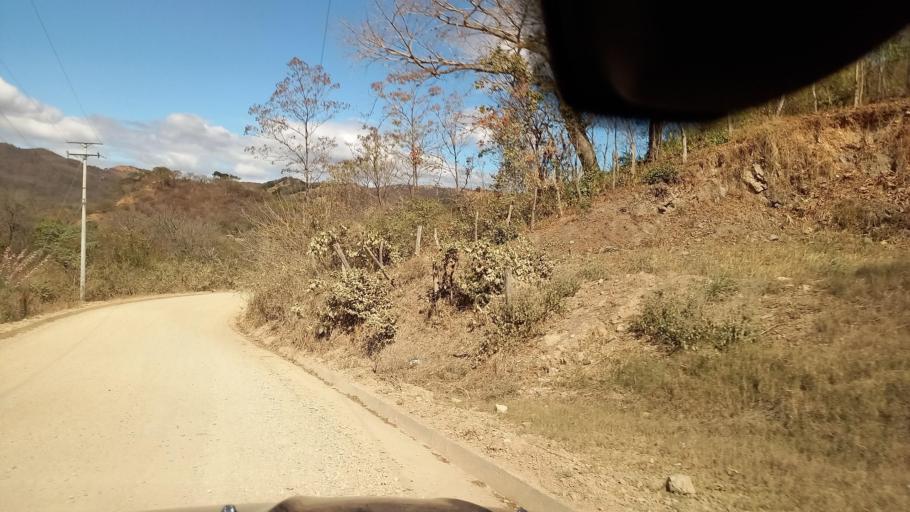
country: SV
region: Santa Ana
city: Metapan
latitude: 14.3595
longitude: -89.4537
